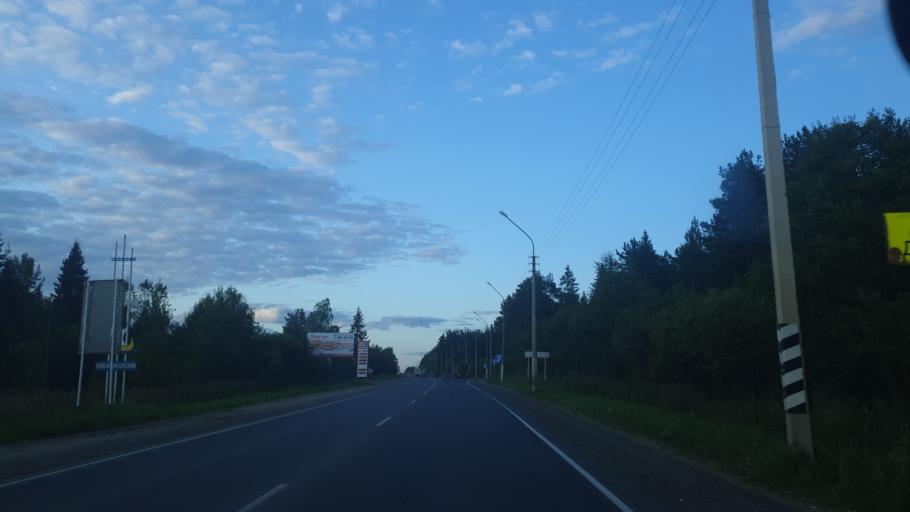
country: RU
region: Komi Republic
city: Verkhnyaya Maksakovka
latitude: 61.6632
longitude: 50.9677
